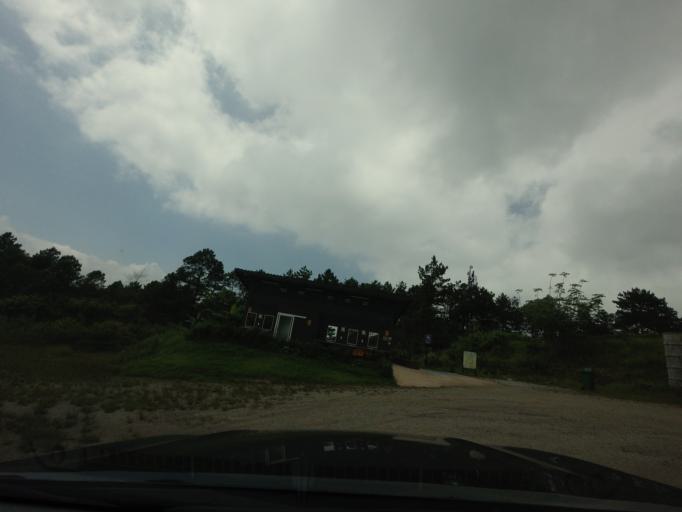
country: TH
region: Loei
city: Phu Ruea
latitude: 17.5076
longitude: 101.3452
